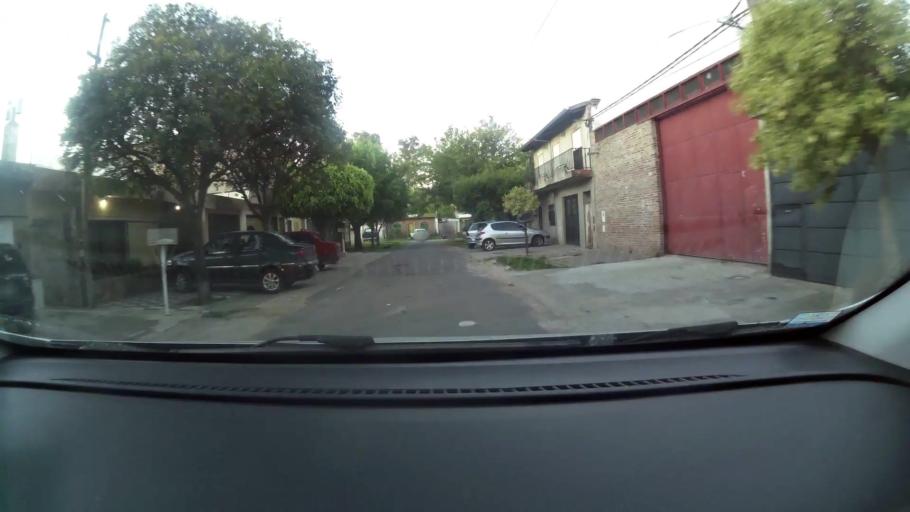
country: AR
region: Santa Fe
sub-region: Departamento de Rosario
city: Rosario
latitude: -32.9627
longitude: -60.6872
